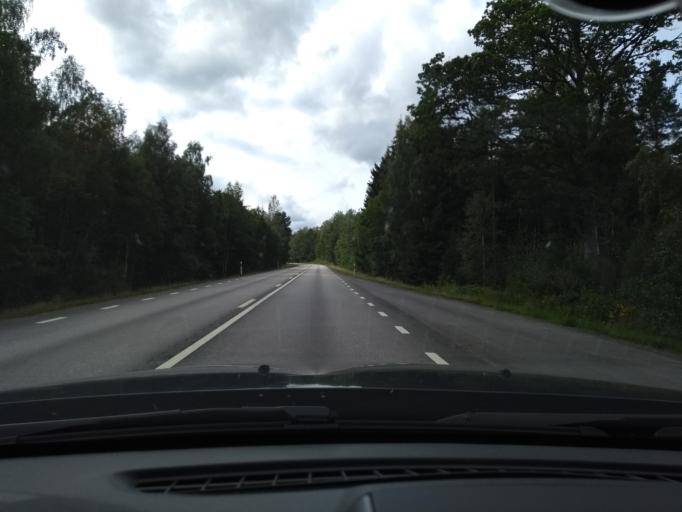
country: SE
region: Kalmar
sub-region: Vimmerby Kommun
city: Vimmerby
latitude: 57.6338
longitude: 15.7285
